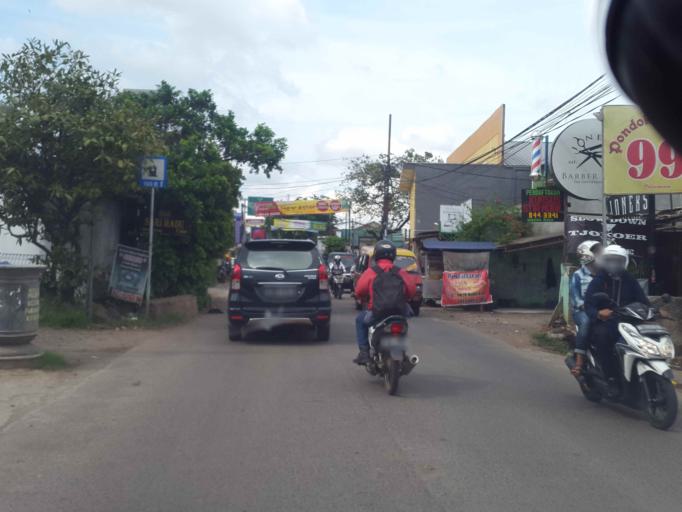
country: ID
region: West Java
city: Cileungsir
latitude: -6.3126
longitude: 106.9247
